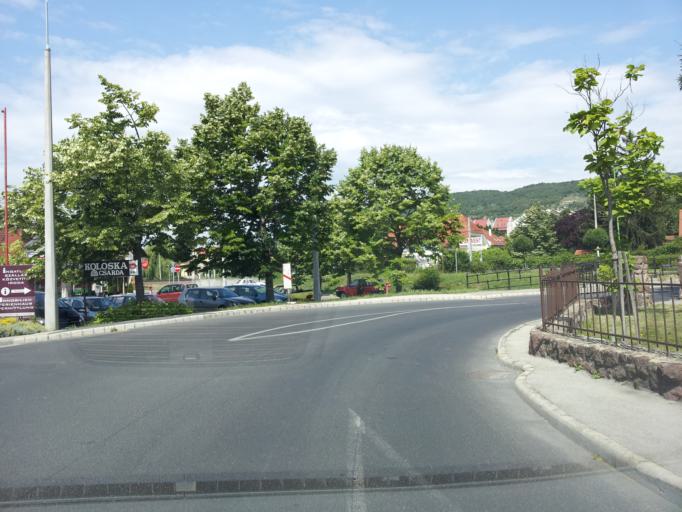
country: HU
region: Veszprem
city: Balatonfured
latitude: 46.9624
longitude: 17.8972
